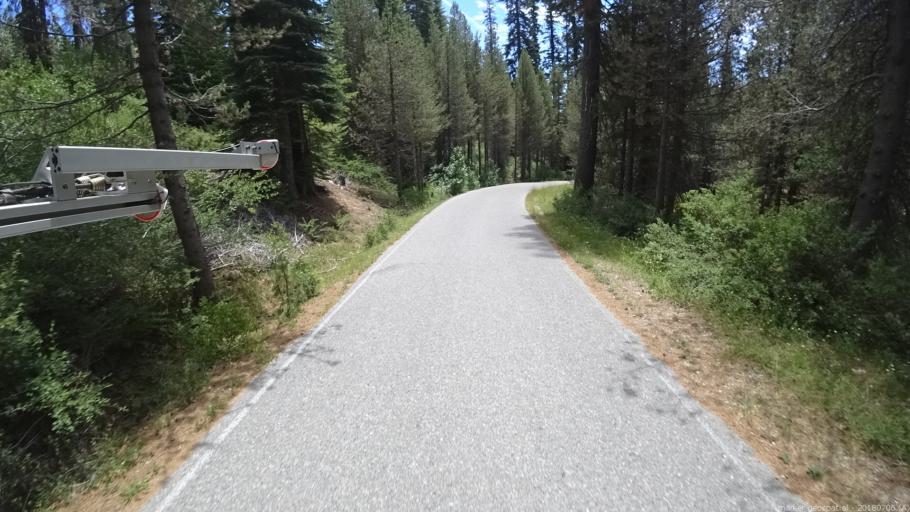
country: US
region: California
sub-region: Madera County
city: Oakhurst
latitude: 37.4354
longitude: -119.4334
